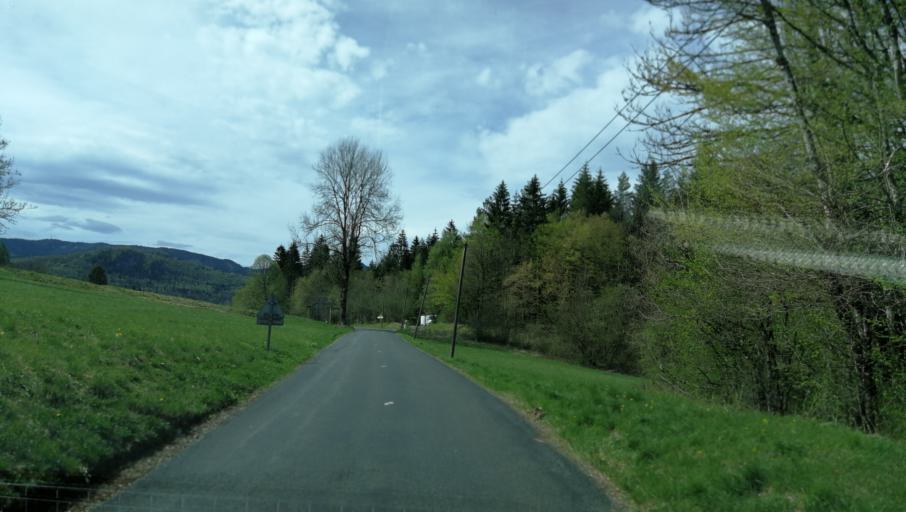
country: FR
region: Rhone-Alpes
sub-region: Departement de l'Ain
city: Chatillon-en-Michaille
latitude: 46.1941
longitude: 5.7428
